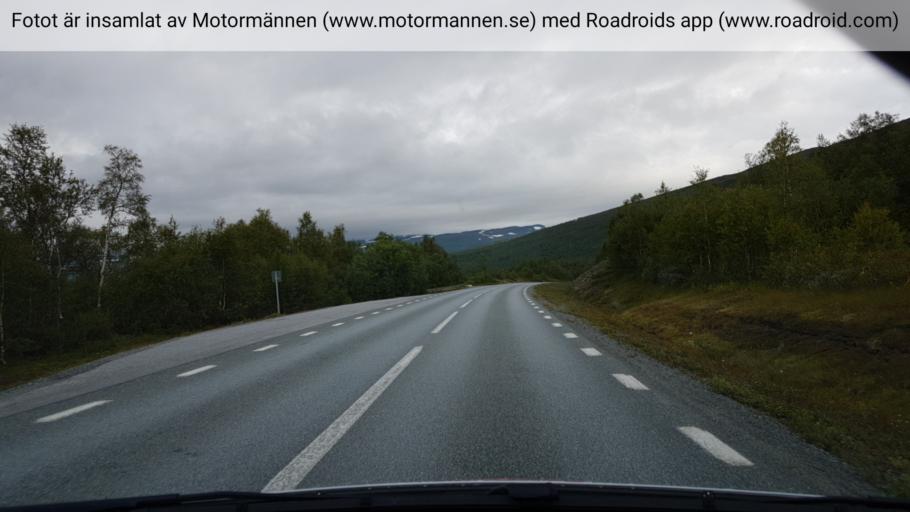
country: NO
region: Nordland
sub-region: Rana
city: Mo i Rana
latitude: 66.0692
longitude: 14.8714
